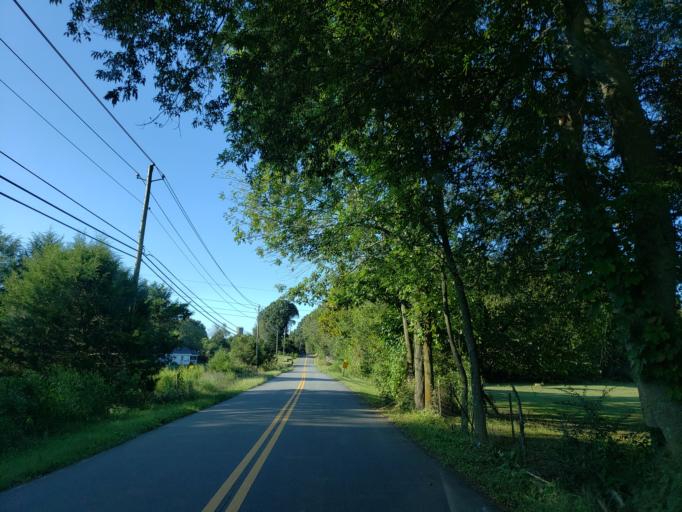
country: US
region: Georgia
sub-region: Bartow County
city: Rydal
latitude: 34.2830
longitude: -84.7505
